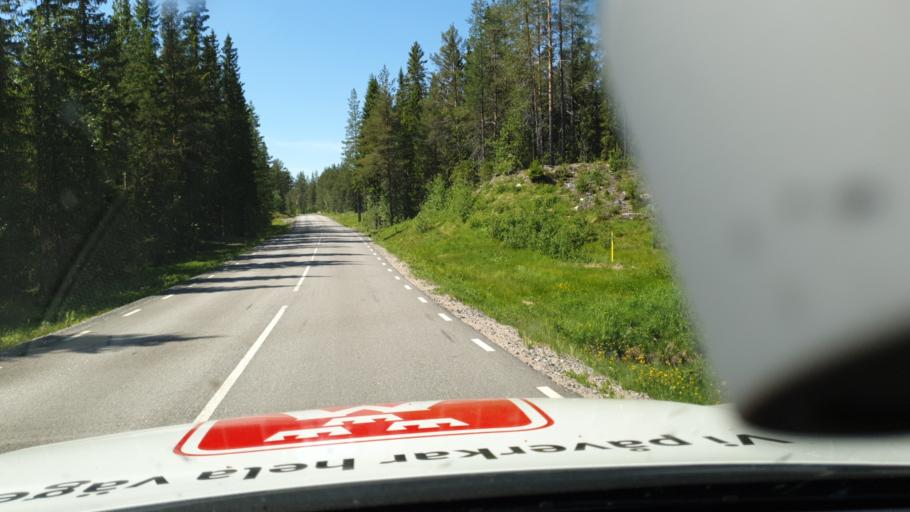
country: SE
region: Jaemtland
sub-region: Harjedalens Kommun
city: Sveg
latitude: 62.0992
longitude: 13.6162
